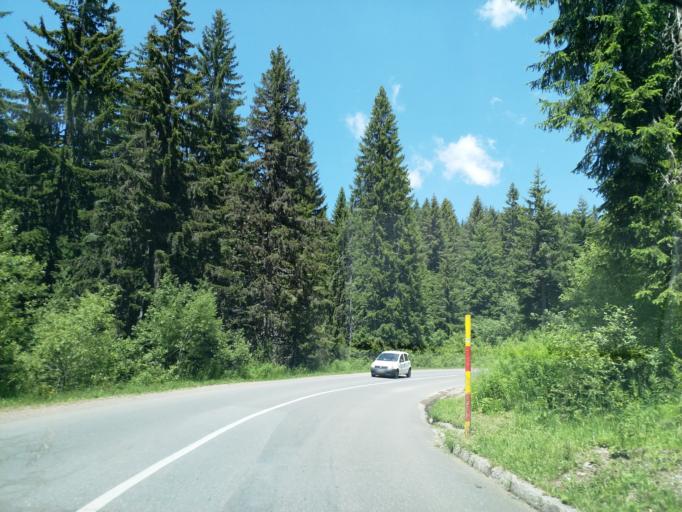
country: XK
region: Mitrovica
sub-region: Komuna e Leposaviqit
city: Leposaviq
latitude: 43.2814
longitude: 20.7958
